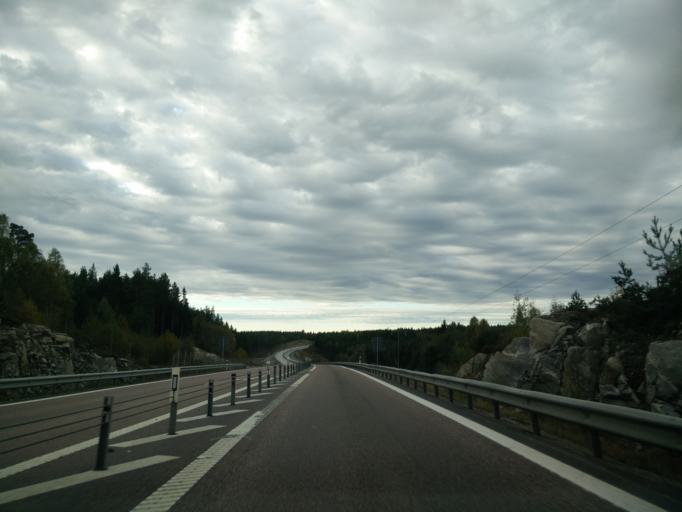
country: SE
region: Gaevleborg
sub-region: Hudiksvalls Kommun
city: Hudiksvall
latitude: 61.7311
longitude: 17.0657
